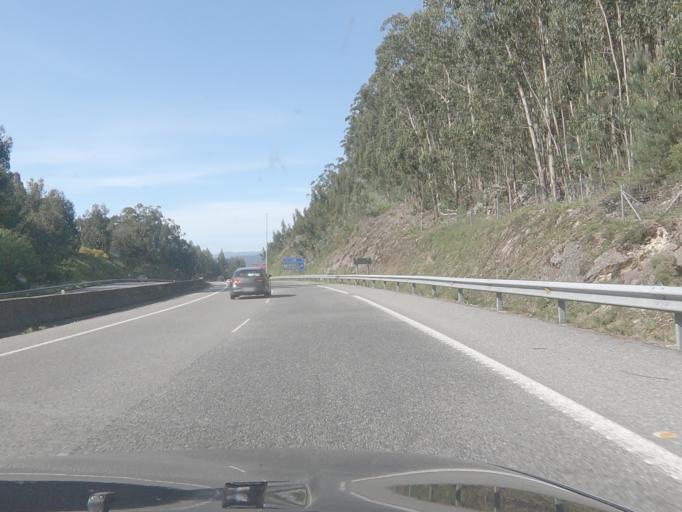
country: ES
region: Galicia
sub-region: Provincia de Pontevedra
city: Meis
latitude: 42.4773
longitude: -8.7709
